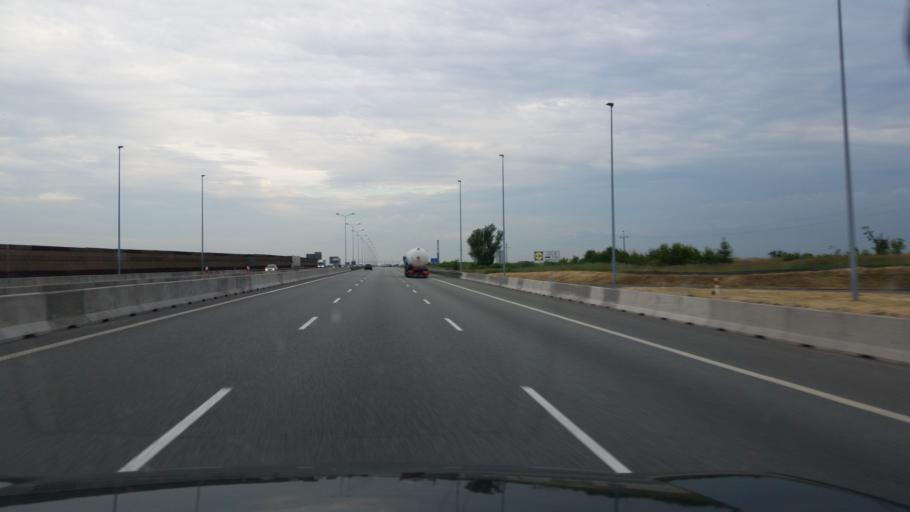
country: PL
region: Silesian Voivodeship
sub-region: Powiat gliwicki
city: Gieraltowice
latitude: 50.2360
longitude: 18.7051
